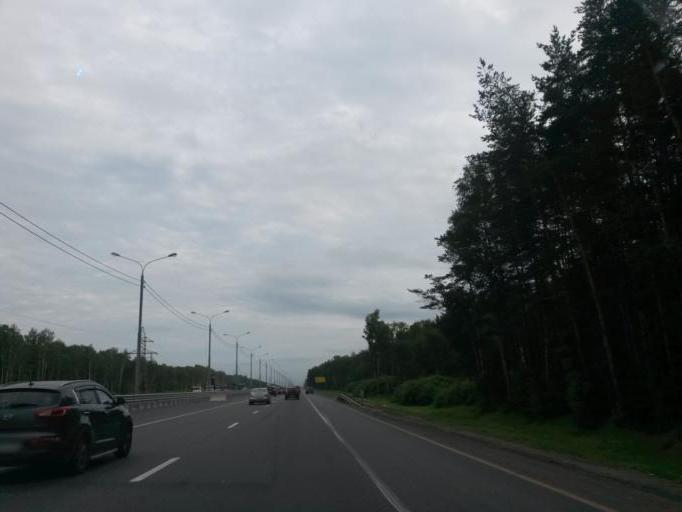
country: RU
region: Moskovskaya
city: L'vovskiy
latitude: 55.2936
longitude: 37.5444
